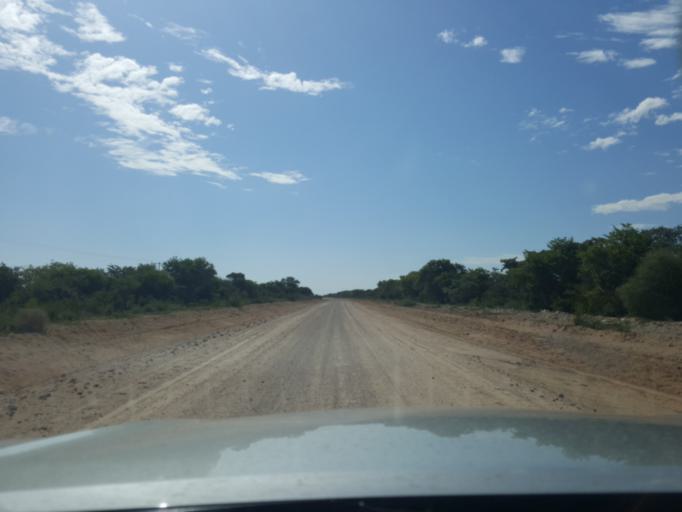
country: BW
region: Kweneng
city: Khudumelapye
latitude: -23.8001
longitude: 24.8027
